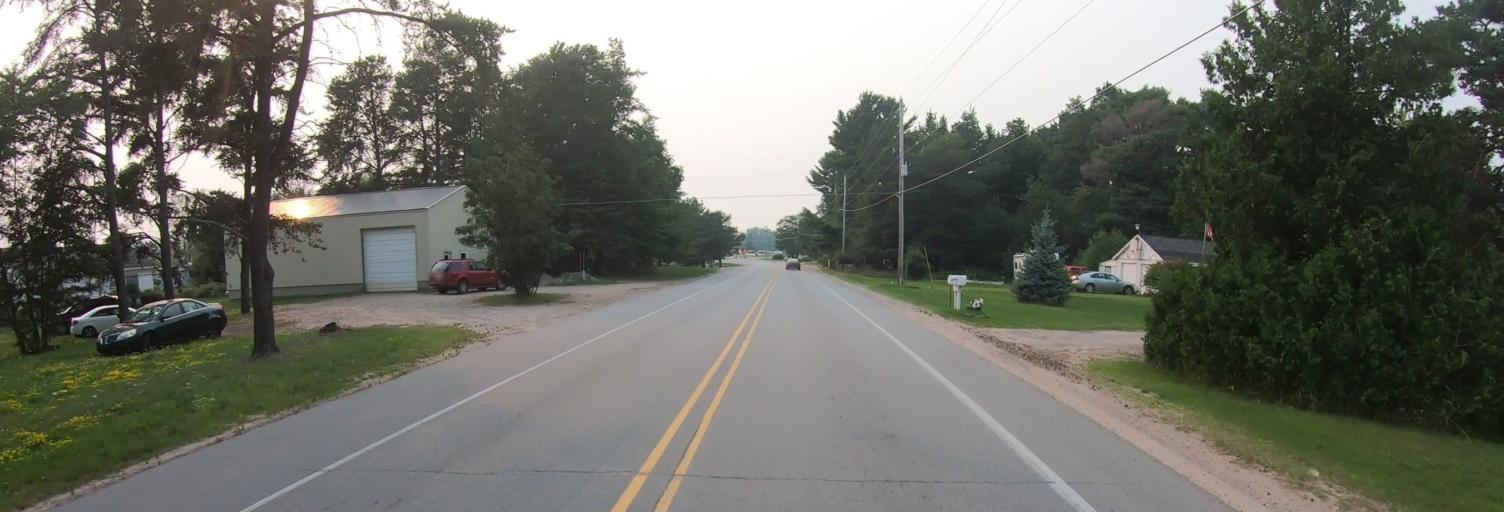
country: US
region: Michigan
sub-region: Chippewa County
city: Sault Ste. Marie
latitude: 46.4526
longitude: -84.6032
